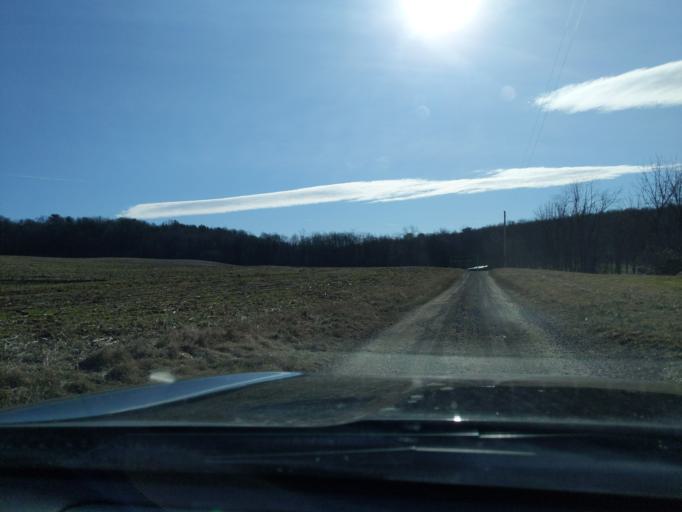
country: US
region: Pennsylvania
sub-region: Blair County
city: Martinsburg
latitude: 40.3908
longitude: -78.2699
